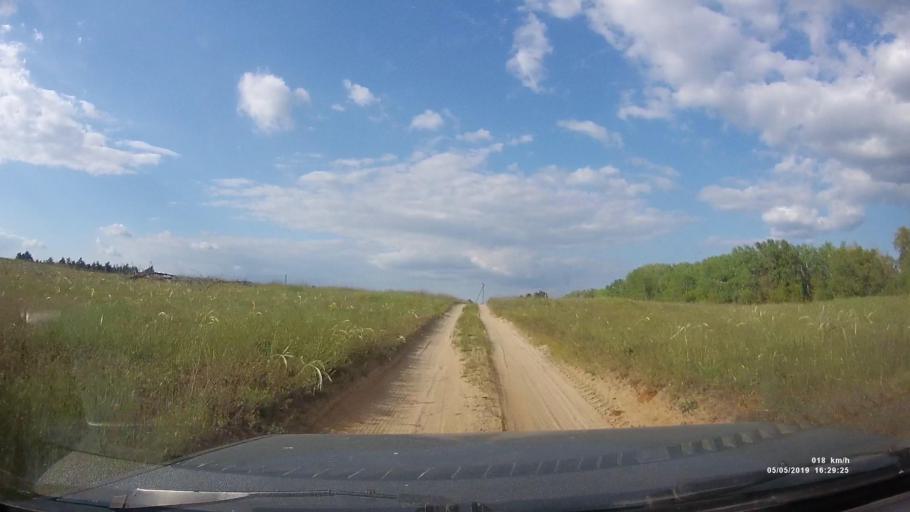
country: RU
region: Rostov
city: Ust'-Donetskiy
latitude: 47.7703
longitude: 41.0142
